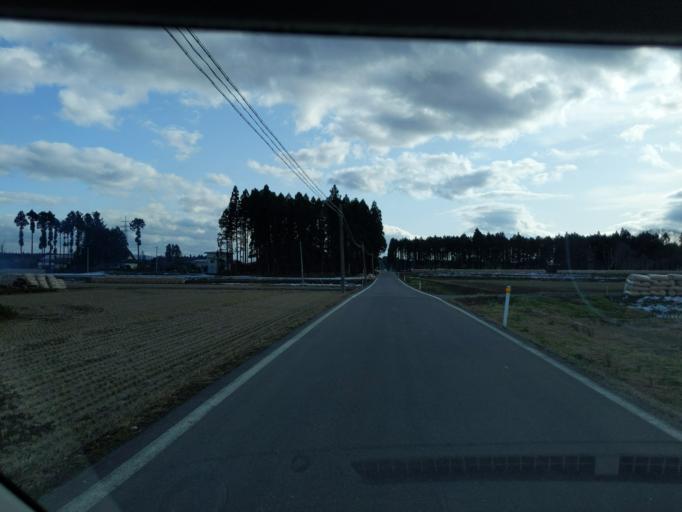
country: JP
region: Iwate
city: Mizusawa
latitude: 39.1249
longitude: 141.0815
